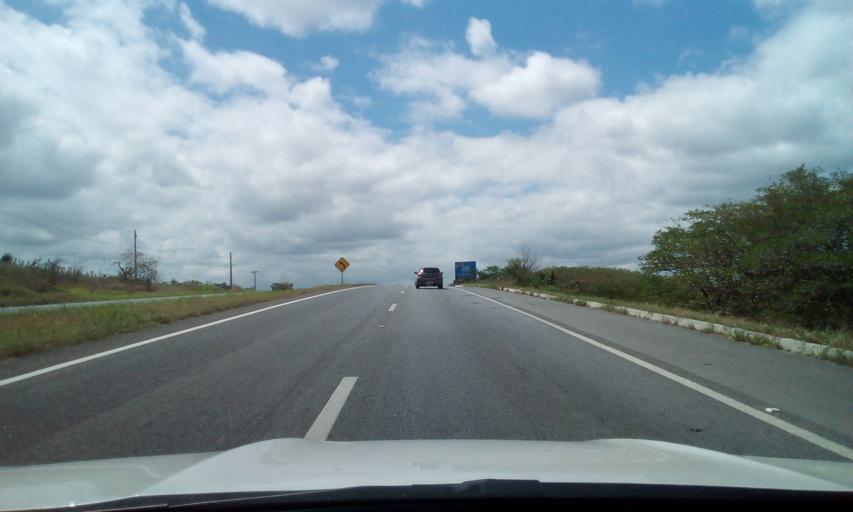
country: BR
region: Paraiba
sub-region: Massaranduba
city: Massaranduba
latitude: -7.2658
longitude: -35.8015
